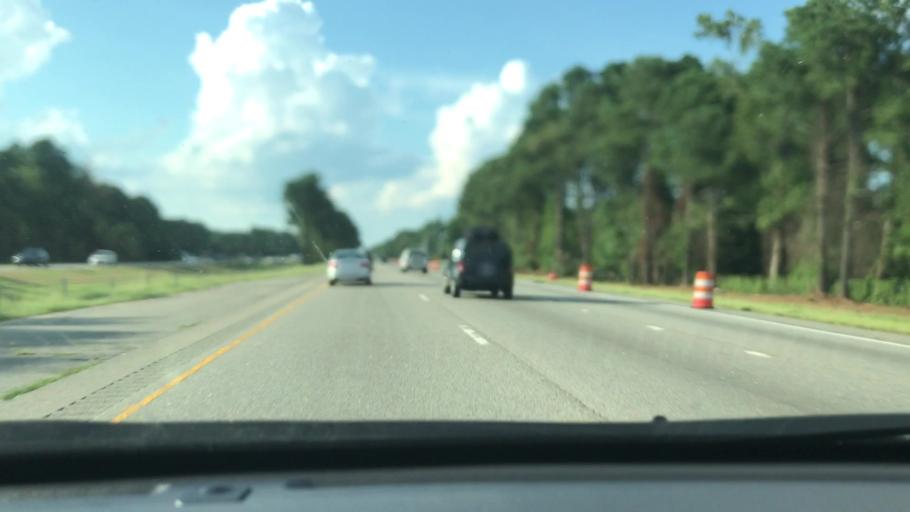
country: US
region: North Carolina
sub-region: Robeson County
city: Lumberton
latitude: 34.7022
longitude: -78.9980
